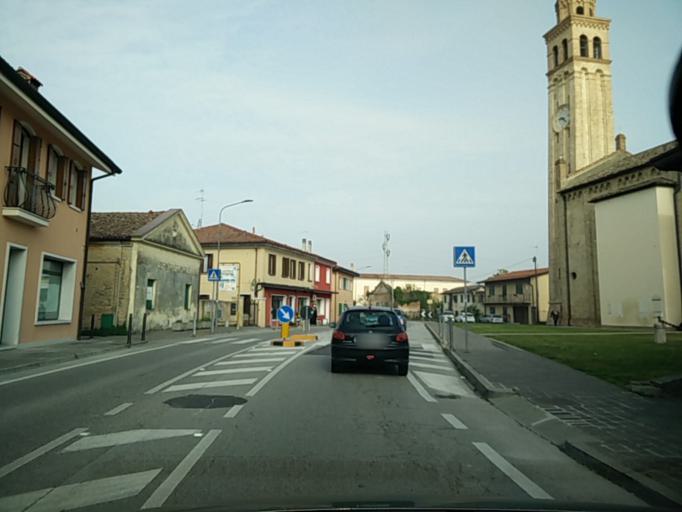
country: IT
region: Veneto
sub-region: Provincia di Venezia
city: Scaltenigo
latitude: 45.4704
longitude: 12.0810
